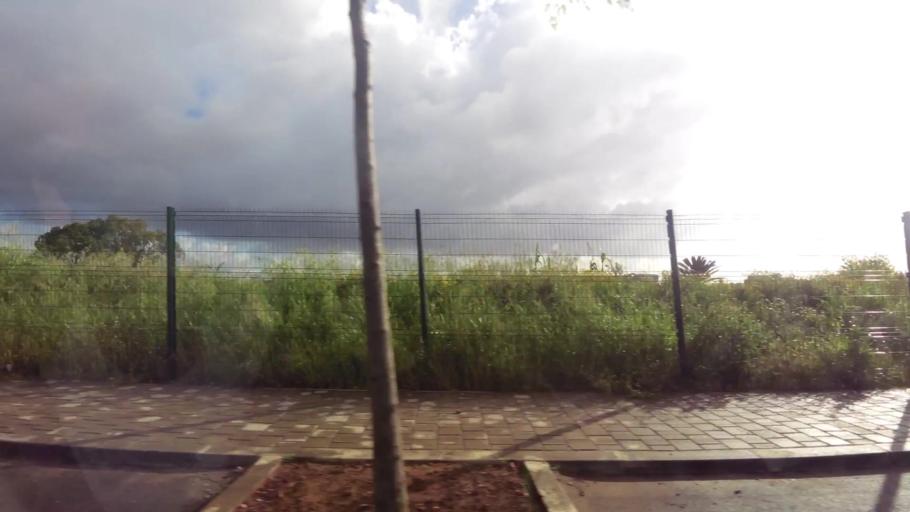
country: MA
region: Grand Casablanca
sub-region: Casablanca
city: Casablanca
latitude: 33.5468
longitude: -7.6566
